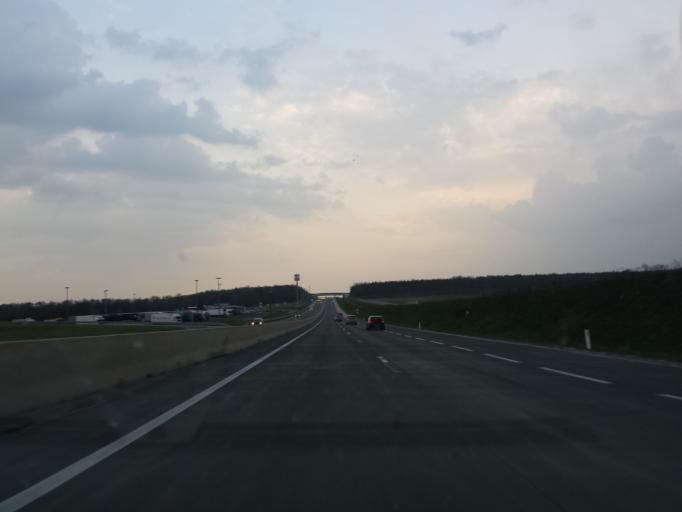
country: AT
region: Lower Austria
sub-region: Politischer Bezirk Mistelbach
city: Hochleithen
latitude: 48.4295
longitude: 16.5498
